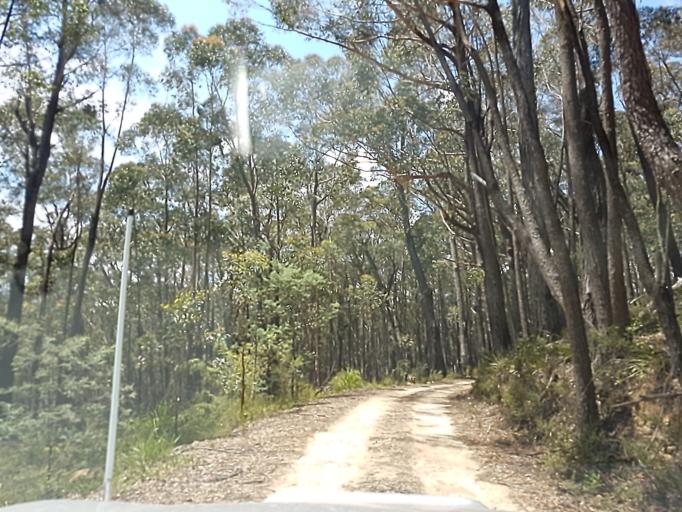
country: AU
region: Victoria
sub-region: East Gippsland
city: Lakes Entrance
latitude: -37.3856
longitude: 148.2795
